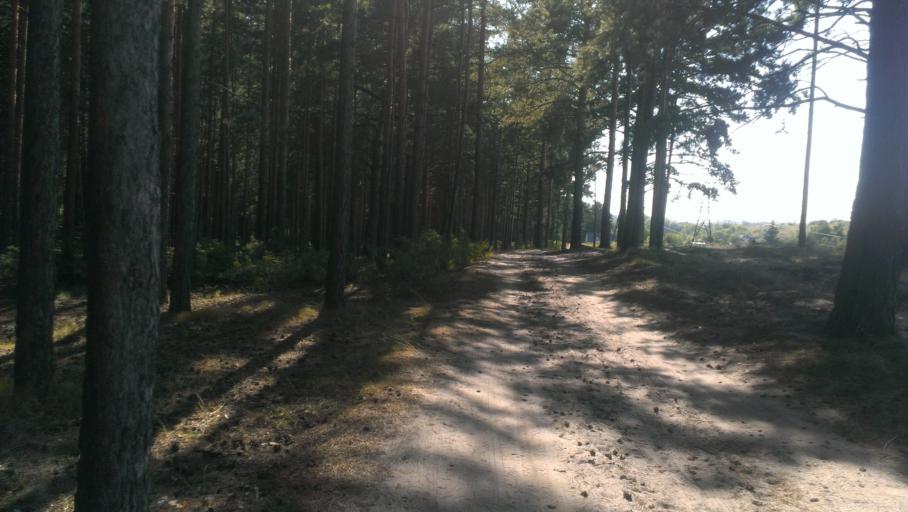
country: RU
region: Altai Krai
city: Novosilikatnyy
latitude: 53.3182
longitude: 83.6821
